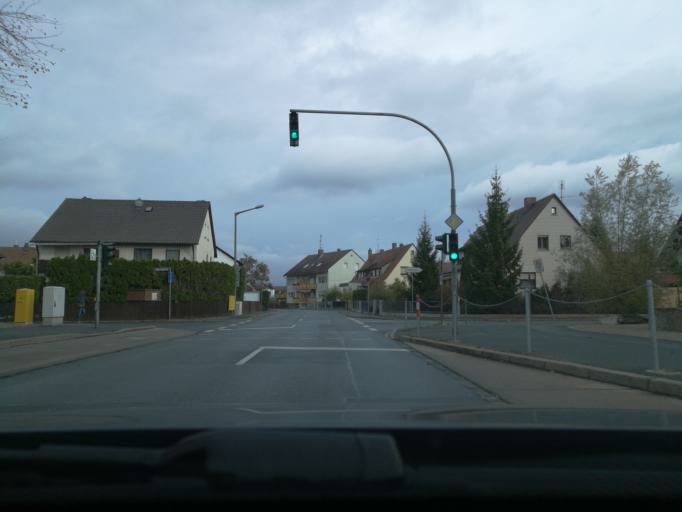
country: DE
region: Bavaria
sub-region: Regierungsbezirk Mittelfranken
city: Furth
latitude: 49.5128
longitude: 10.9787
